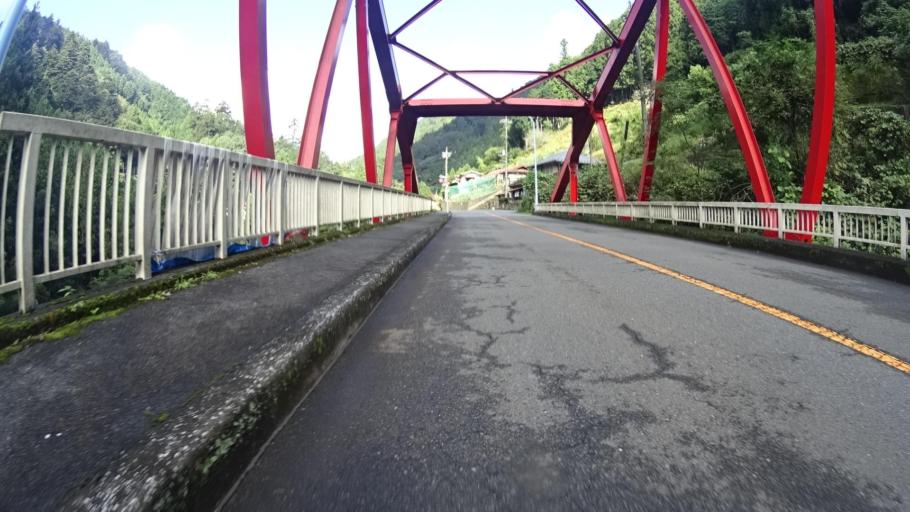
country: JP
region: Tokyo
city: Itsukaichi
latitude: 35.7317
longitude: 139.1035
